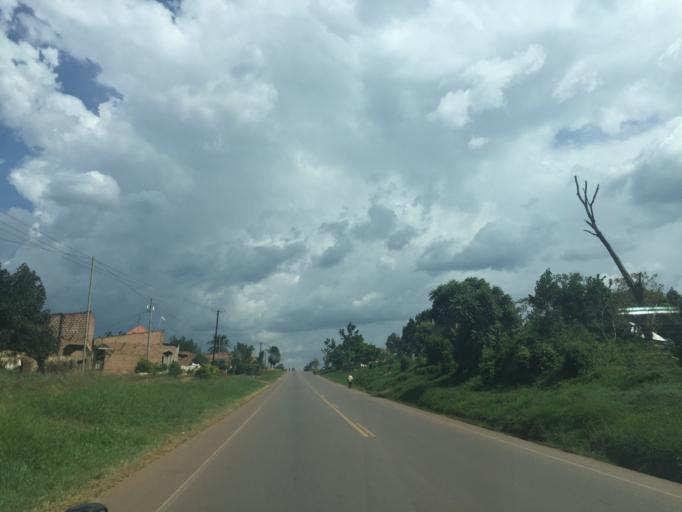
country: UG
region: Central Region
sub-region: Luwero District
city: Wobulenzi
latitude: 0.7361
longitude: 32.5220
